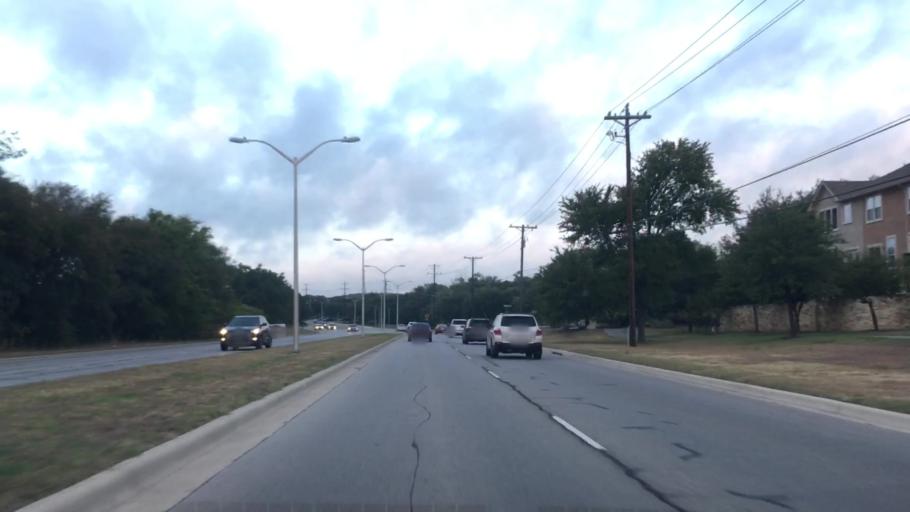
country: US
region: Texas
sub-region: Williamson County
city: Cedar Park
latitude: 30.5064
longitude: -97.7971
